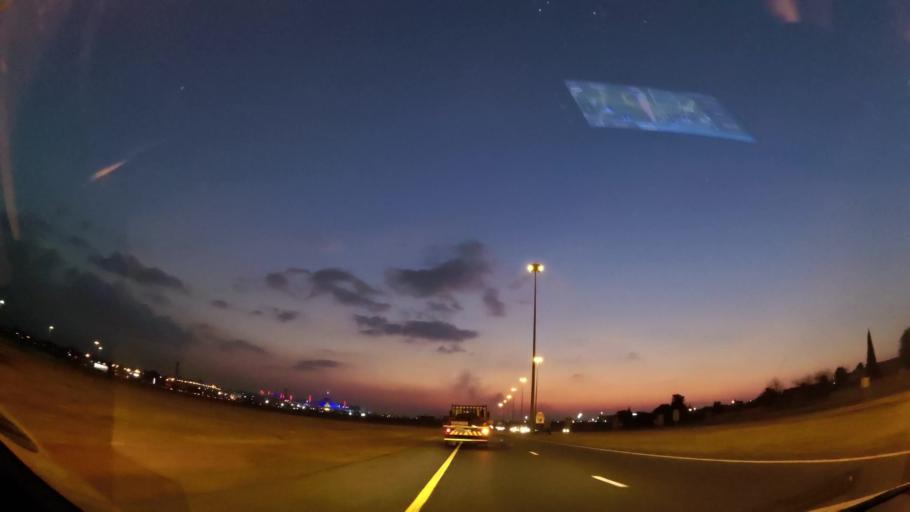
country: ZA
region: Gauteng
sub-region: Ekurhuleni Metropolitan Municipality
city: Brakpan
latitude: -26.2563
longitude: 28.3260
